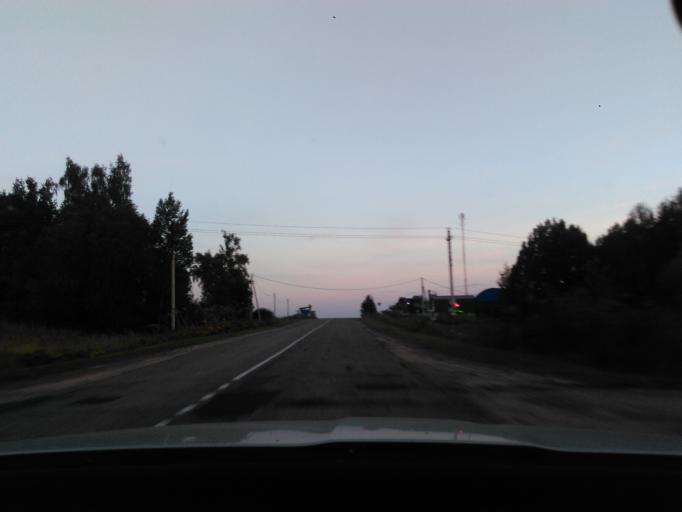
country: RU
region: Moskovskaya
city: Klin
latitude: 56.2333
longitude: 36.7493
